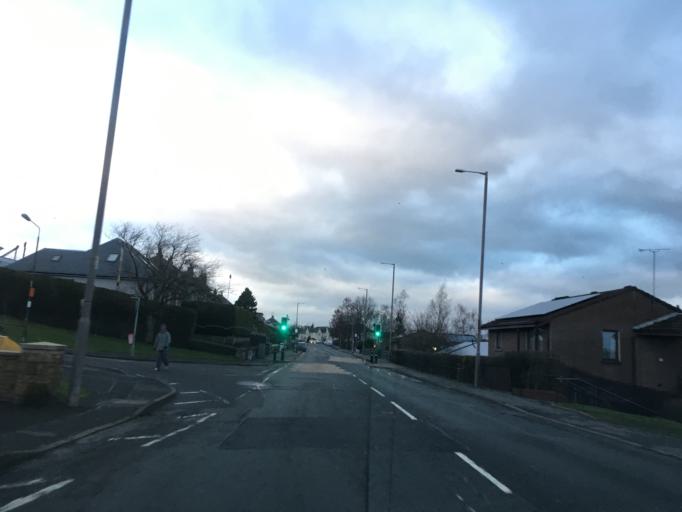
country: GB
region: Scotland
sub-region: Stirling
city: Bannockburn
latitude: 56.0977
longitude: -3.9275
